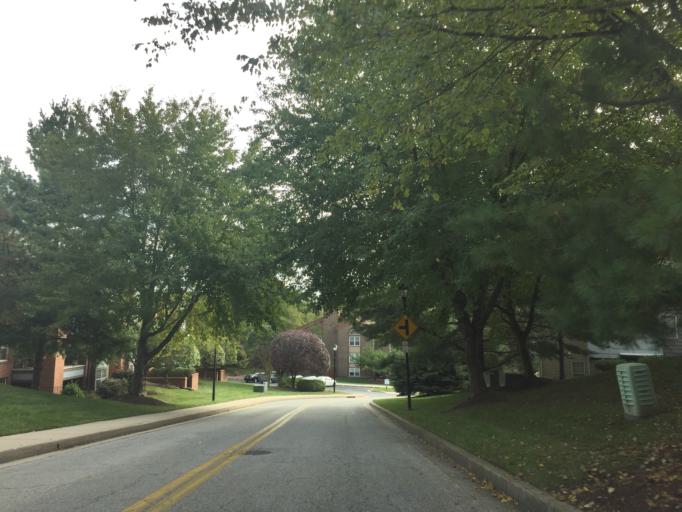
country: US
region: Maryland
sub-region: Baltimore County
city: Pikesville
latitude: 39.3817
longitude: -76.6711
